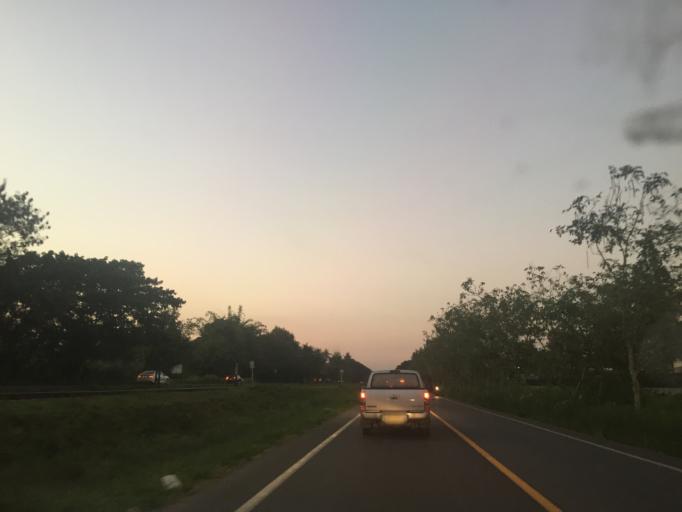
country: TH
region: Chiang Mai
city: Saraphi
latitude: 18.7032
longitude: 99.0450
